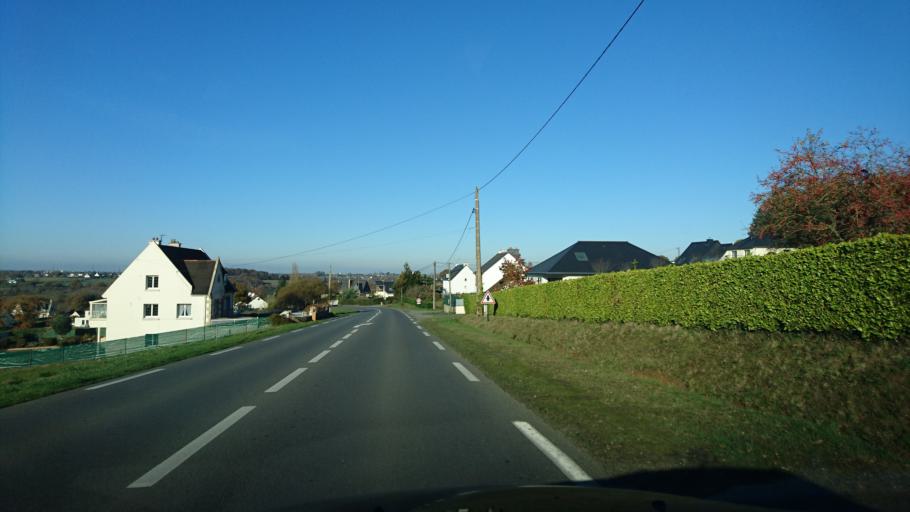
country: FR
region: Brittany
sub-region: Departement des Cotes-d'Armor
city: Pledran
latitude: 48.4546
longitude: -2.7531
